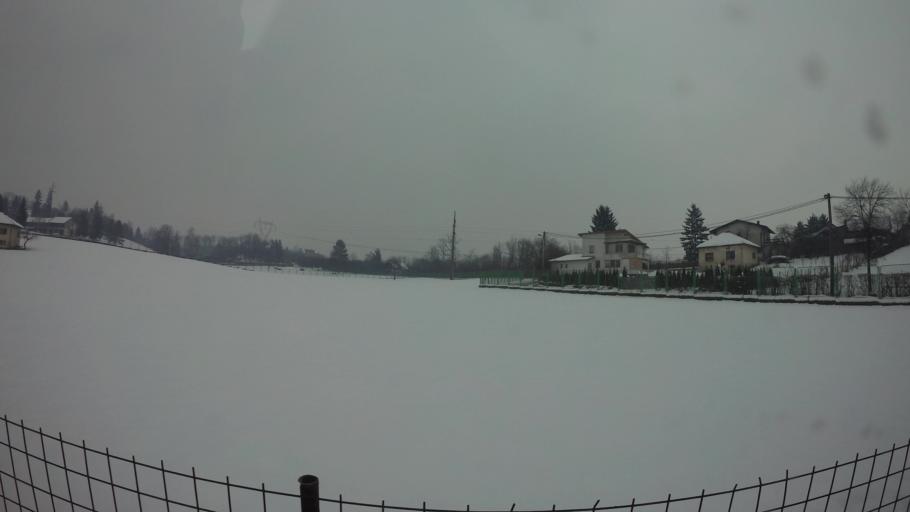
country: BA
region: Federation of Bosnia and Herzegovina
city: Hadzici
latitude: 43.8426
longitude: 18.2655
